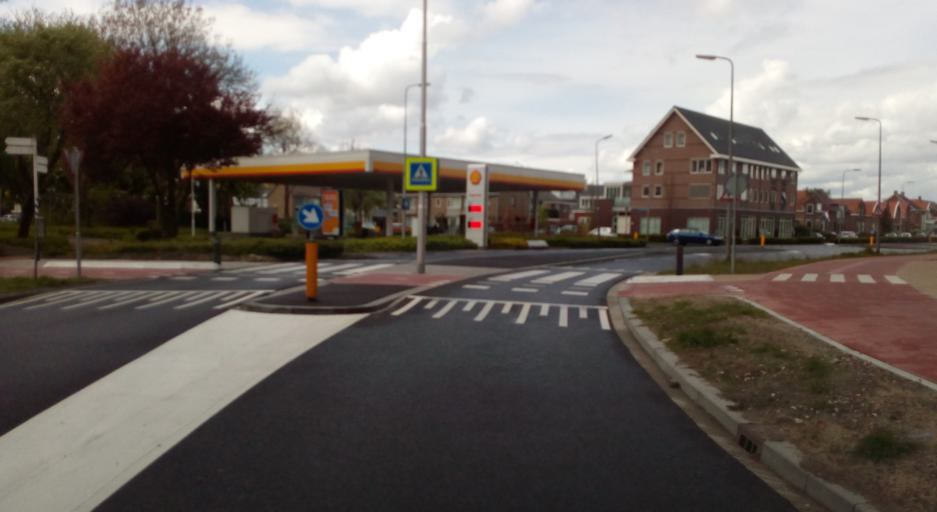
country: NL
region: South Holland
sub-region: Gemeente Zwijndrecht
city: Zwijndrecht
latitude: 51.8251
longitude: 4.6389
